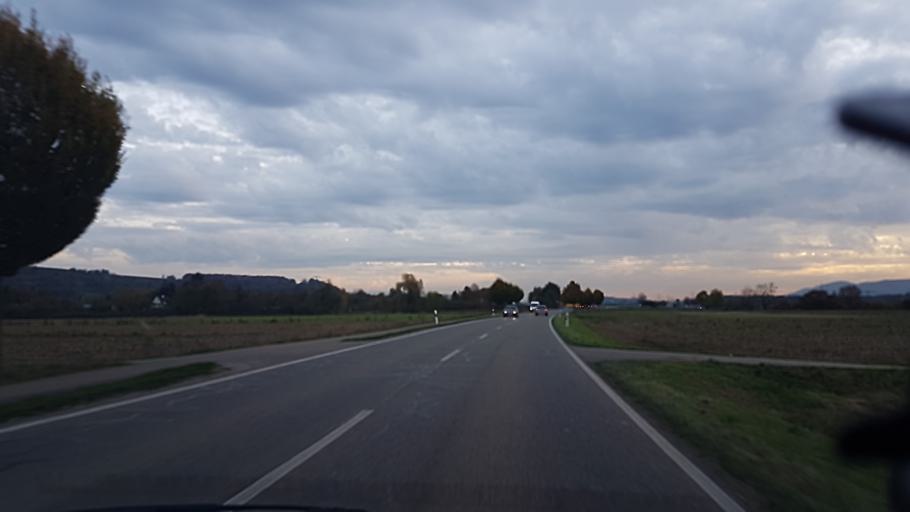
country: DE
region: Baden-Wuerttemberg
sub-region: Freiburg Region
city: Kenzingen
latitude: 48.1910
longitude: 7.7604
